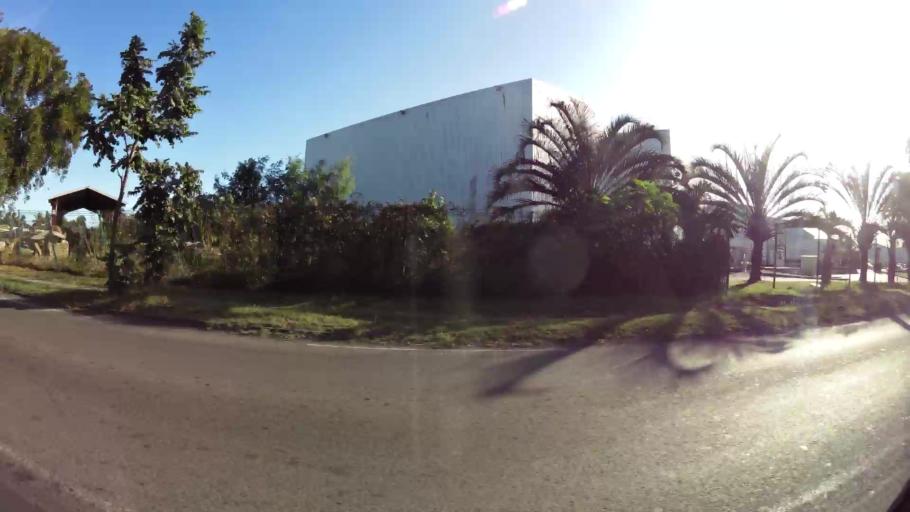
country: RE
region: Reunion
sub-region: Reunion
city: Saint-Louis
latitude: -21.2756
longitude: 55.3729
